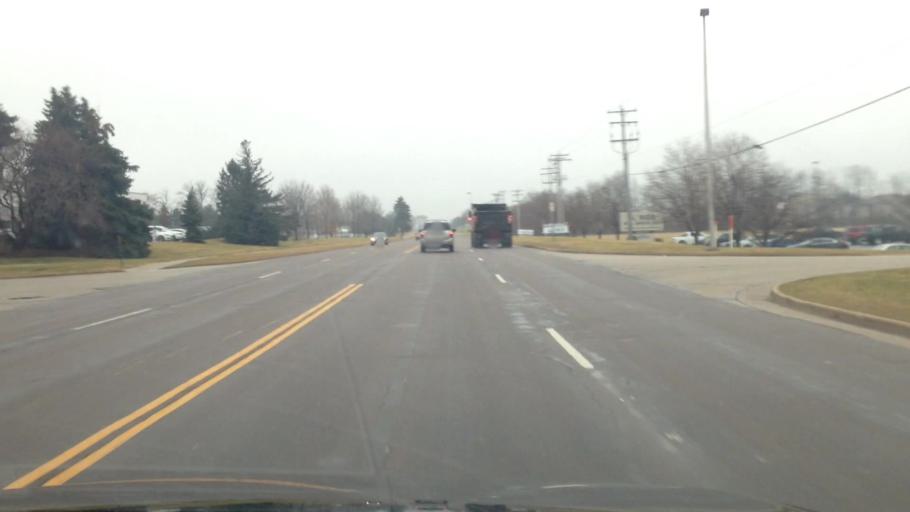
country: US
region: Wisconsin
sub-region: Washington County
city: Germantown
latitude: 43.2311
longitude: -88.1428
